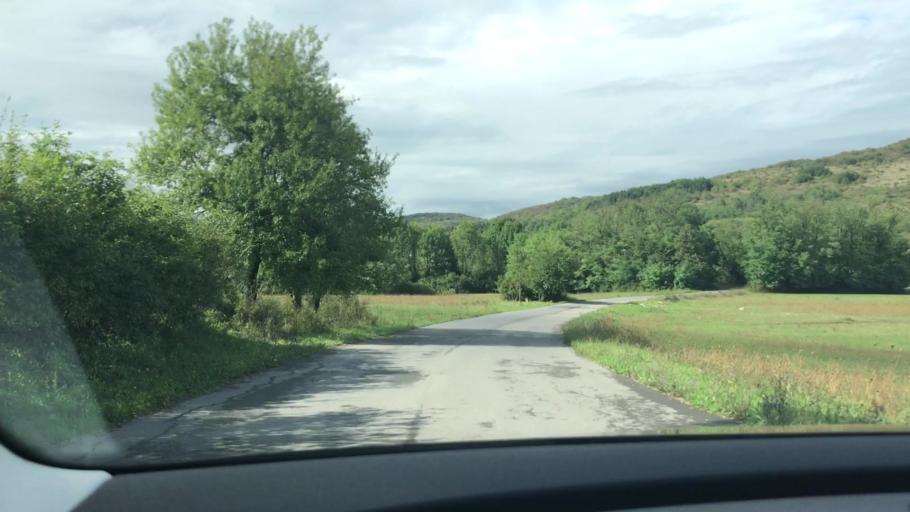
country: BA
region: Federation of Bosnia and Herzegovina
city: Izacic
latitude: 44.8729
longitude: 15.7173
